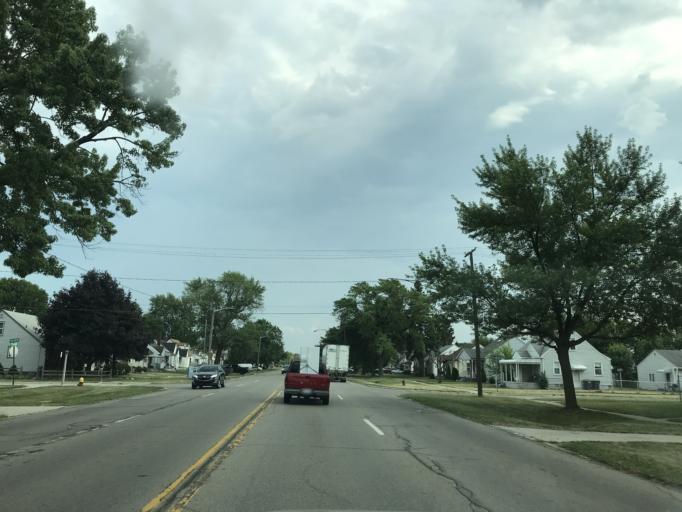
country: US
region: Michigan
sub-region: Wayne County
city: Allen Park
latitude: 42.2593
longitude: -83.2314
